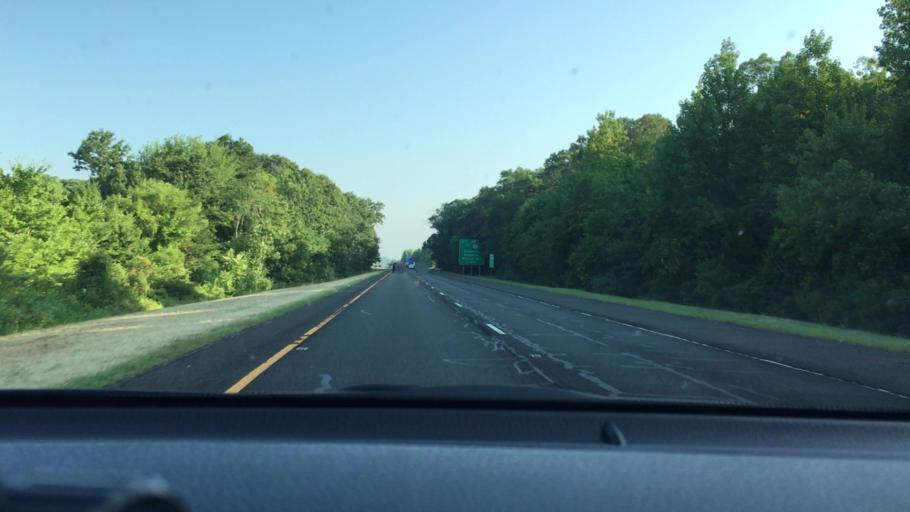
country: US
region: New Jersey
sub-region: Gloucester County
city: Richwood
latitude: 39.7037
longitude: -75.1514
